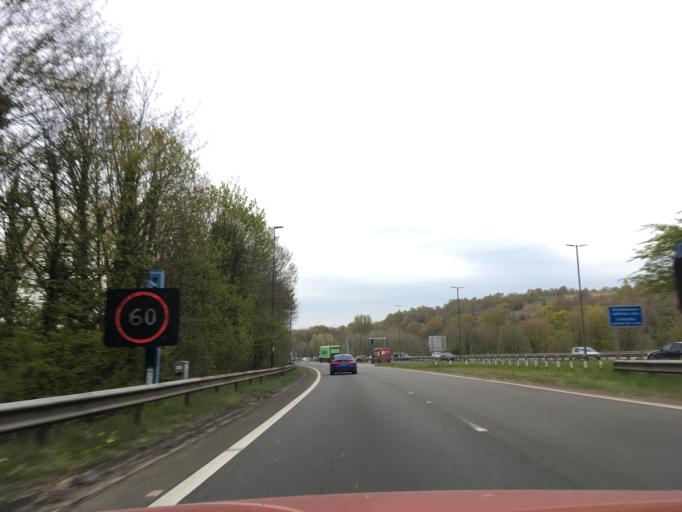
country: GB
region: Wales
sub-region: Newport
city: Newport
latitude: 51.5708
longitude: -3.0342
